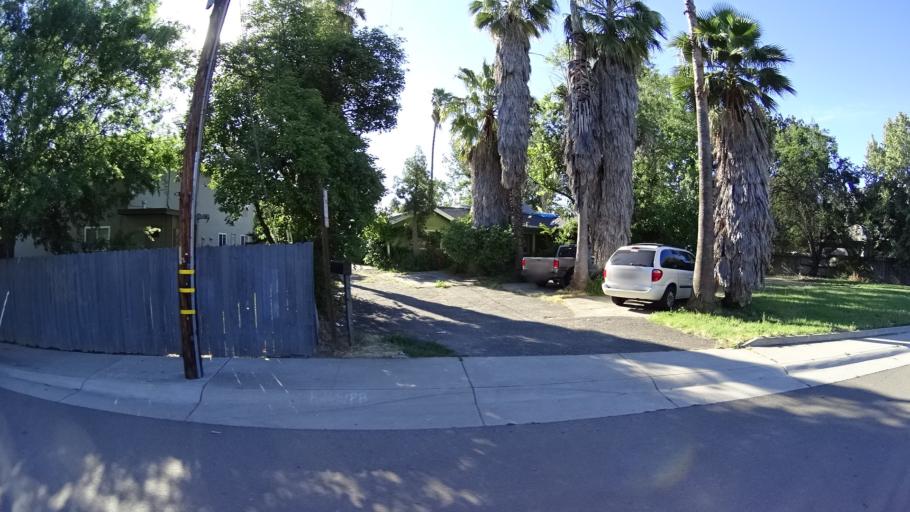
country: US
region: California
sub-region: Sacramento County
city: Arden-Arcade
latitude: 38.6360
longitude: -121.3791
